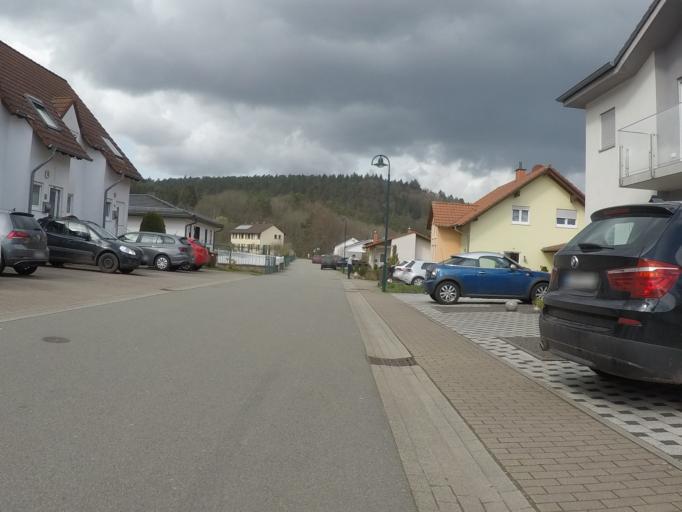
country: DE
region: Rheinland-Pfalz
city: Munchweiler an der Rodalbe
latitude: 49.2213
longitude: 7.6973
